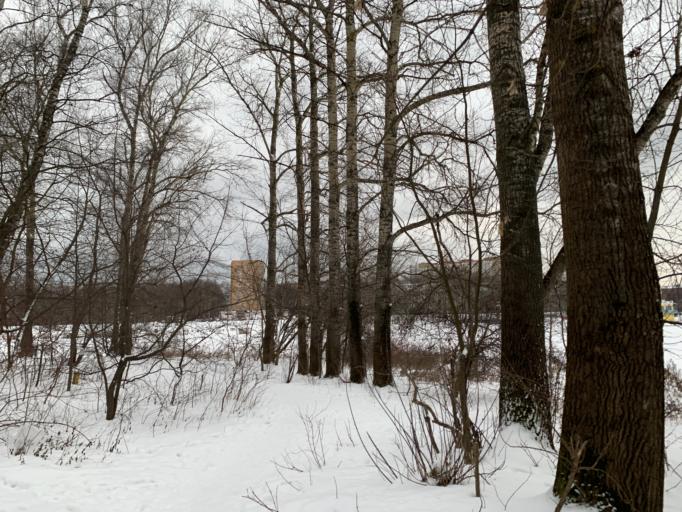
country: RU
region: Moskovskaya
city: Pushkino
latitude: 56.0026
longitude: 37.8670
